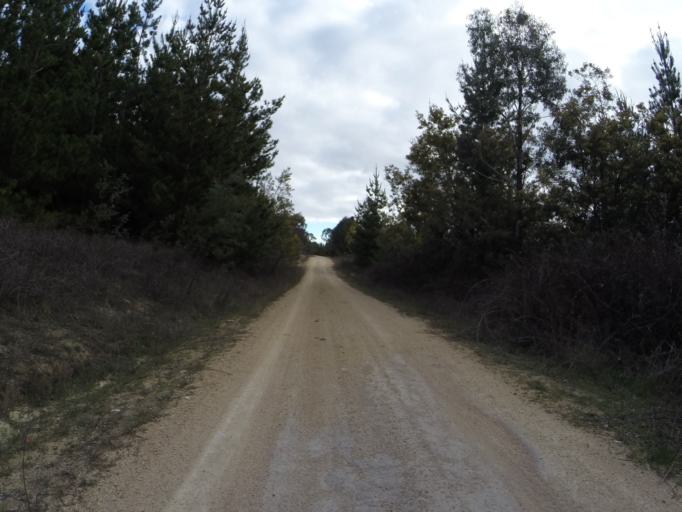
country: AU
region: Australian Capital Territory
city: Macquarie
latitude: -35.3443
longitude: 148.9320
